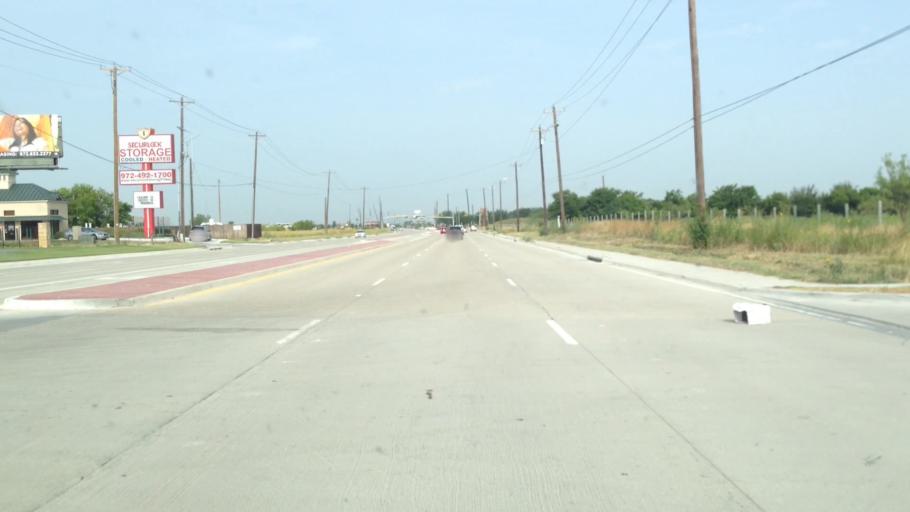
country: US
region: Texas
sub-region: Denton County
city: The Colony
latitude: 33.0449
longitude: -96.8691
